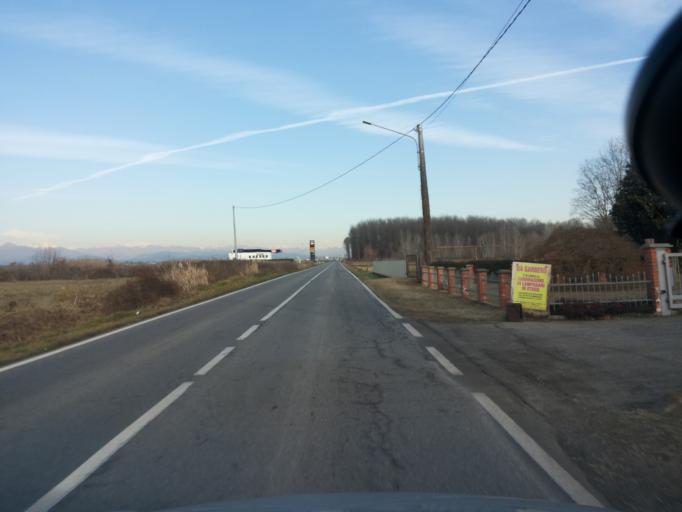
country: IT
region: Piedmont
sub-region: Provincia di Vercelli
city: Greggio
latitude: 45.4667
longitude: 8.3865
